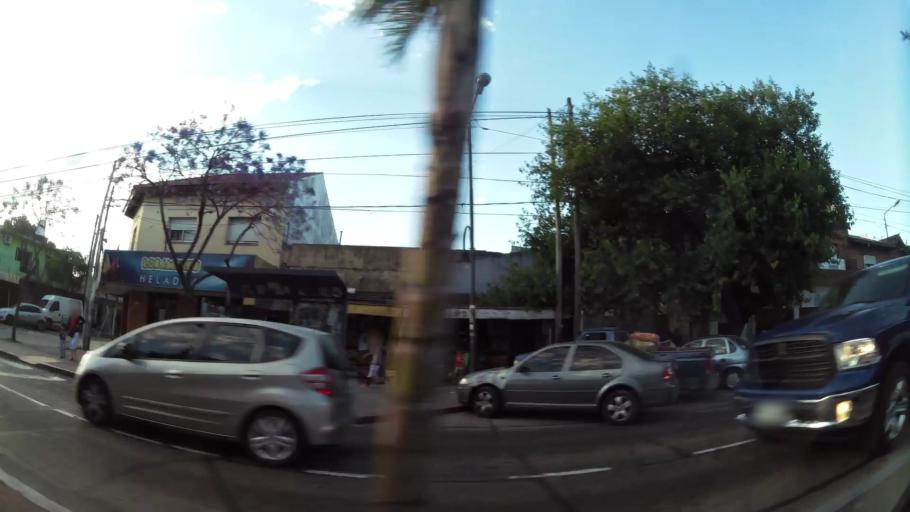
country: AR
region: Buenos Aires
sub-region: Partido de Tigre
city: Tigre
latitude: -34.4595
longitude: -58.5701
